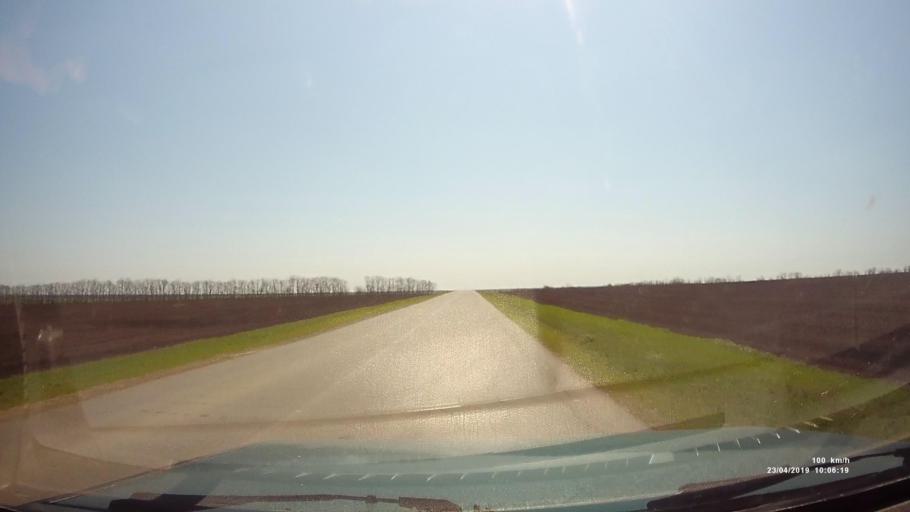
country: RU
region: Rostov
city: Sovetskoye
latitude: 46.7345
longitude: 42.2336
